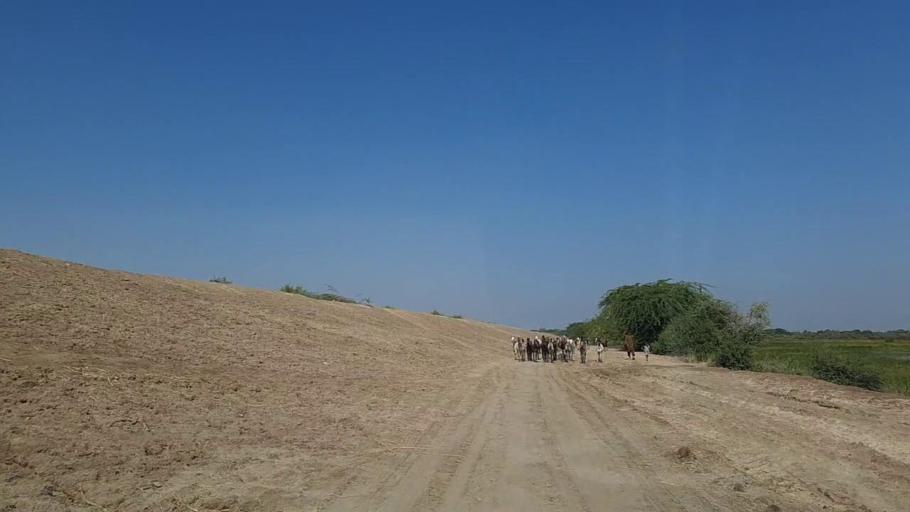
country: PK
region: Sindh
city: Chuhar Jamali
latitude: 24.4835
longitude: 68.0141
